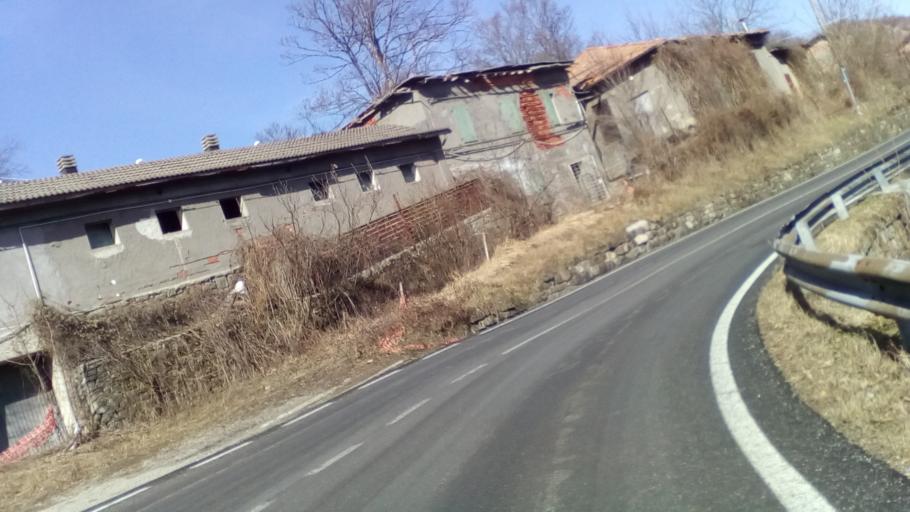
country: IT
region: Emilia-Romagna
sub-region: Provincia di Modena
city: Riolunato
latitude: 44.2325
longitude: 10.6252
